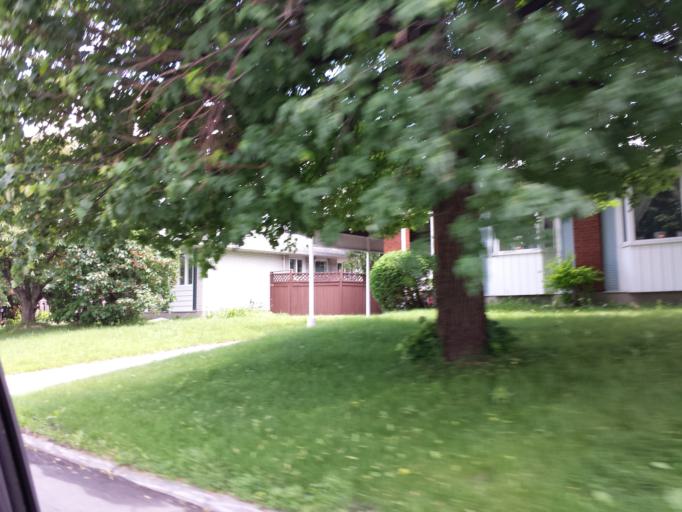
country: CA
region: Ontario
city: Bells Corners
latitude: 45.3503
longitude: -75.7817
